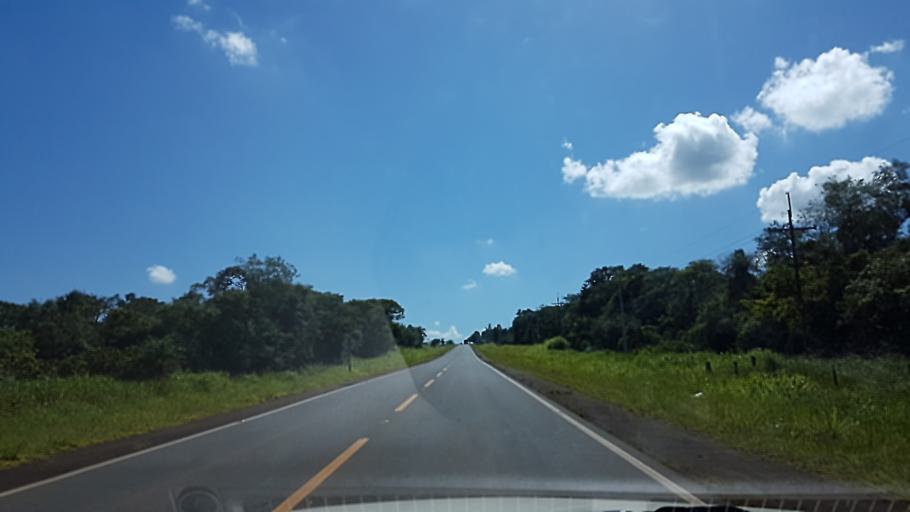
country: PY
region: Itapua
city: Carmen del Parana
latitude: -27.2094
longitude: -56.0794
